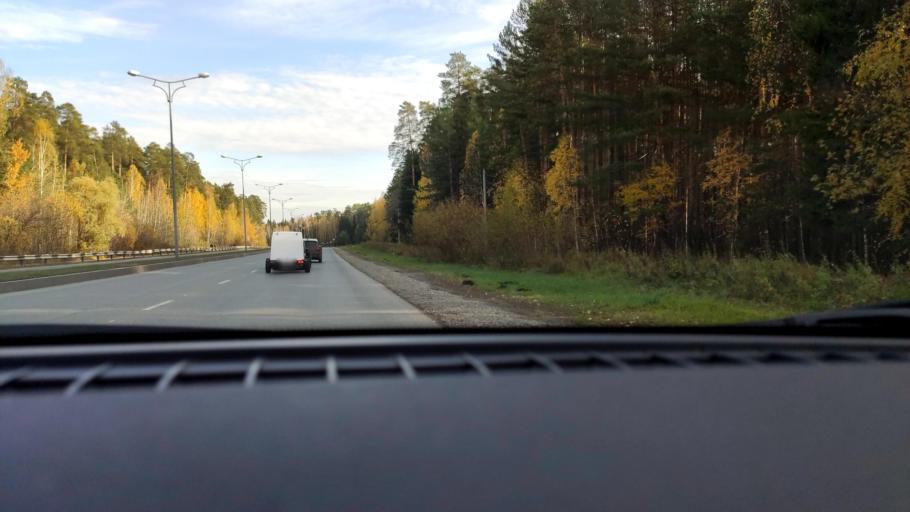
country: RU
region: Perm
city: Kondratovo
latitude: 58.0189
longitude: 55.9884
